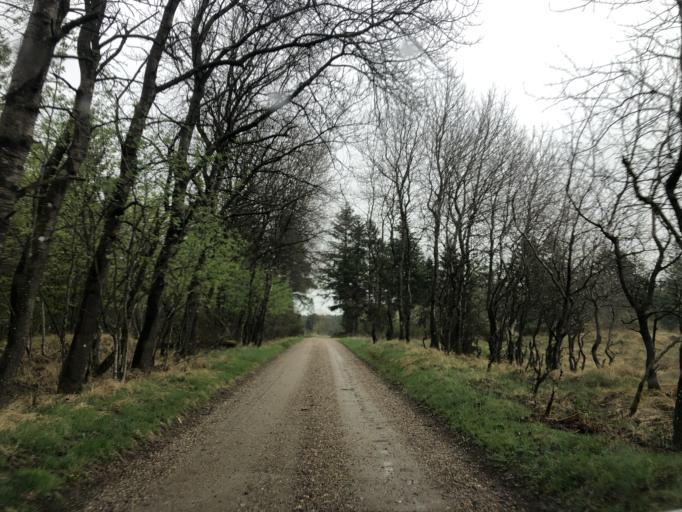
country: DK
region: Central Jutland
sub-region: Lemvig Kommune
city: Lemvig
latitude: 56.4491
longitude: 8.3892
